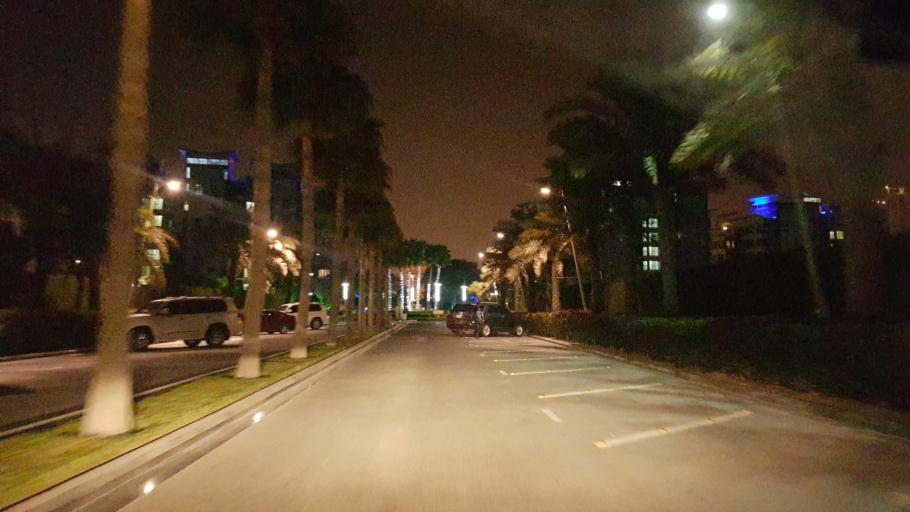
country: BH
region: Manama
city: Jidd Hafs
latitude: 26.2381
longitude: 50.5650
